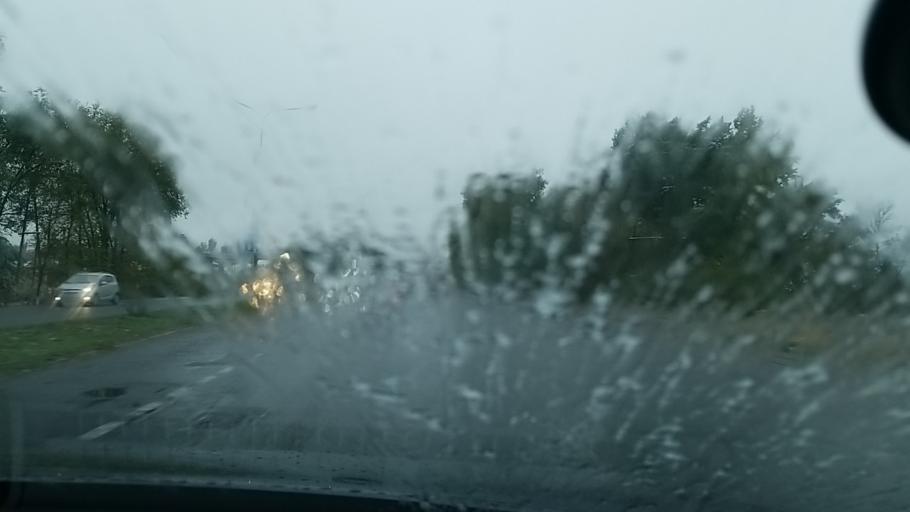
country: KZ
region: Almaty Oblysy
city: Burunday
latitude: 43.2153
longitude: 76.6947
